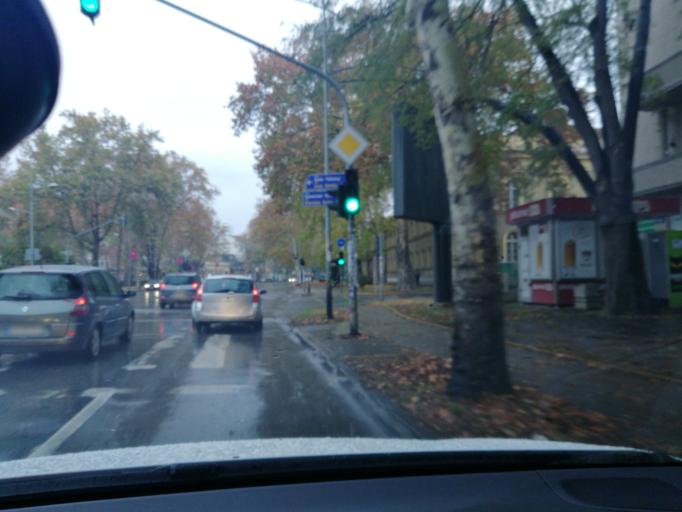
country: RS
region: Autonomna Pokrajina Vojvodina
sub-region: Juznobacki Okrug
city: Novi Sad
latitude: 45.2500
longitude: 19.8329
